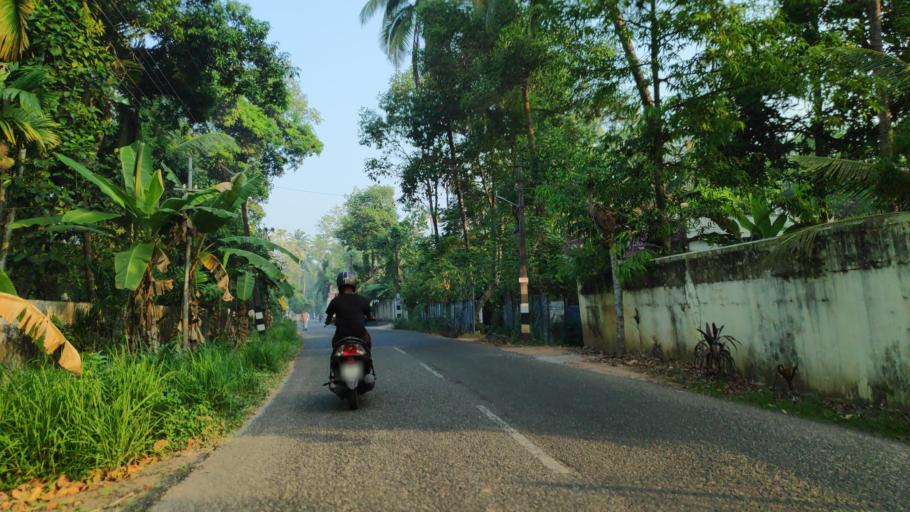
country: IN
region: Kerala
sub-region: Alappuzha
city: Vayalar
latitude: 9.7002
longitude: 76.2898
